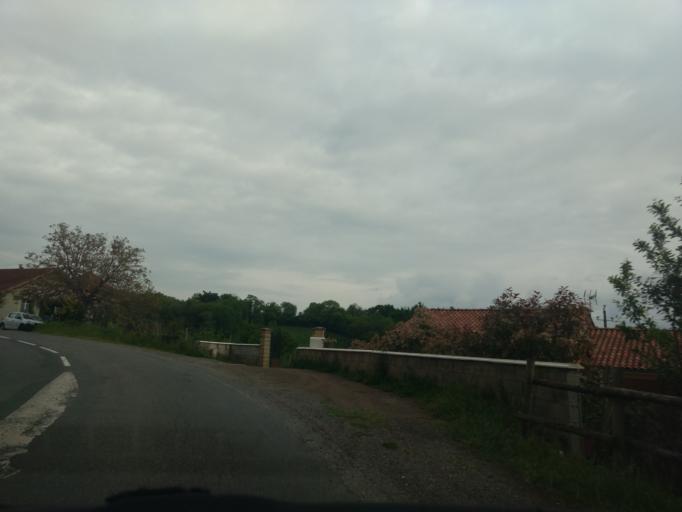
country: FR
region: Midi-Pyrenees
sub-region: Departement de l'Aveyron
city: Viviez
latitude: 44.5460
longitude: 2.1505
